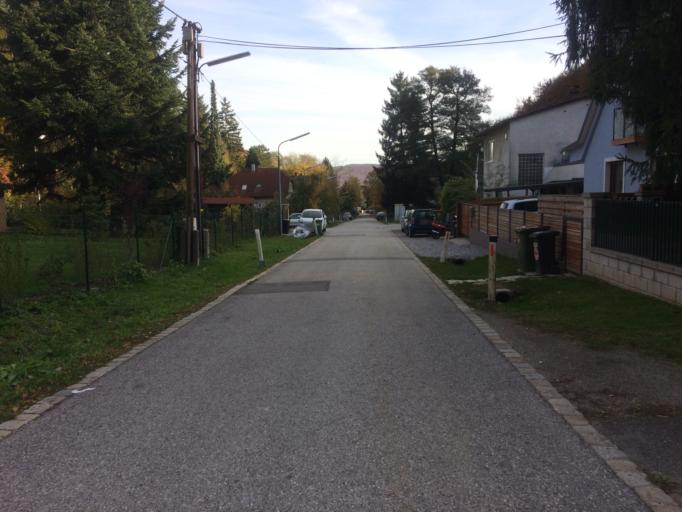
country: AT
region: Lower Austria
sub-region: Politischer Bezirk Wien-Umgebung
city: Purkersdorf
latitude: 48.2127
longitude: 16.2044
